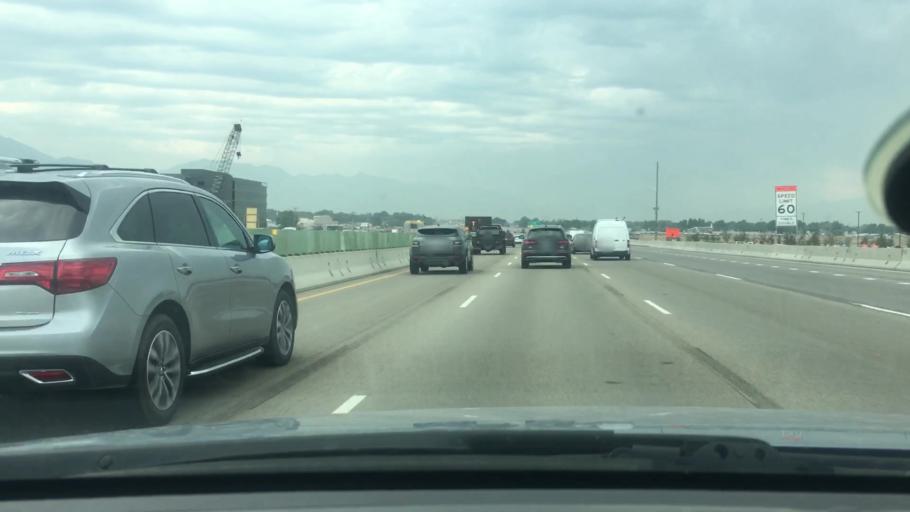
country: US
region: Utah
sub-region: Utah County
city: Lehi
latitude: 40.4217
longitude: -111.8805
